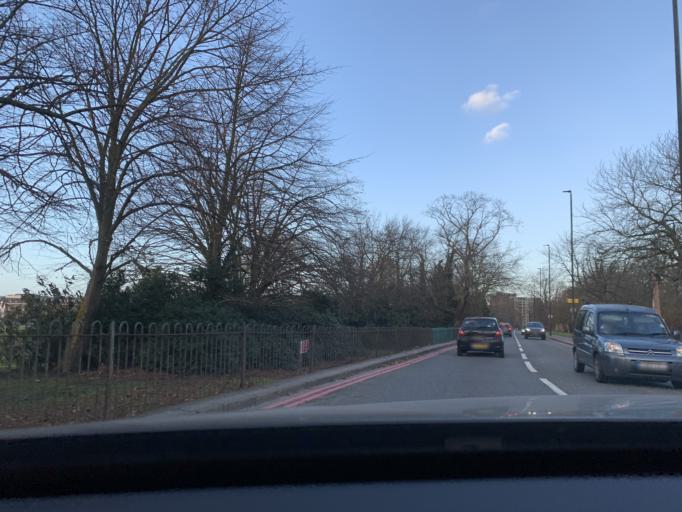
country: GB
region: England
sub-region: Greater London
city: Woolwich
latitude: 51.4838
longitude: 0.0621
